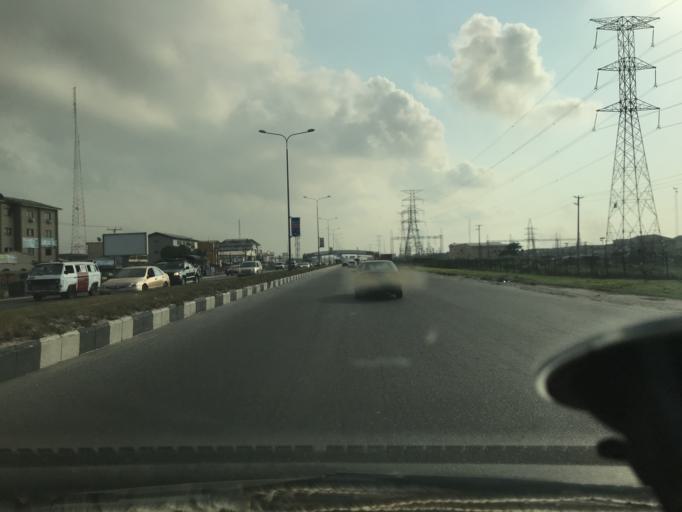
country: NG
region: Lagos
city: Ikoyi
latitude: 6.4355
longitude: 3.4999
